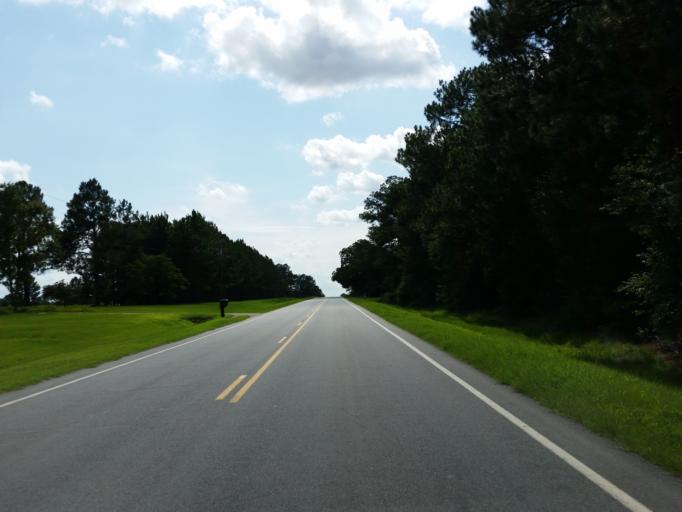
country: US
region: Georgia
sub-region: Turner County
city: Ashburn
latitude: 31.6589
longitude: -83.5755
